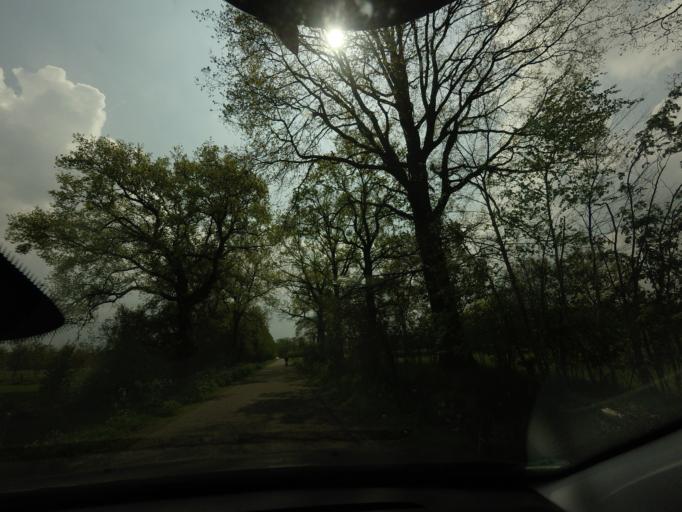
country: NL
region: Overijssel
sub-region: Gemeente Haaksbergen
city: Haaksbergen
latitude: 52.1804
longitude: 6.8078
